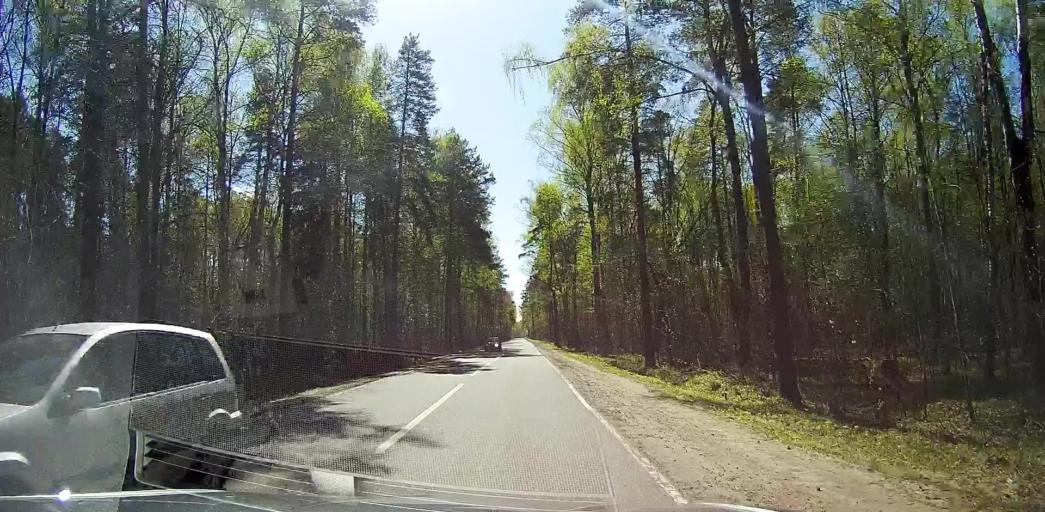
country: RU
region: Moskovskaya
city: Beloozerskiy
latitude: 55.4838
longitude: 38.4254
